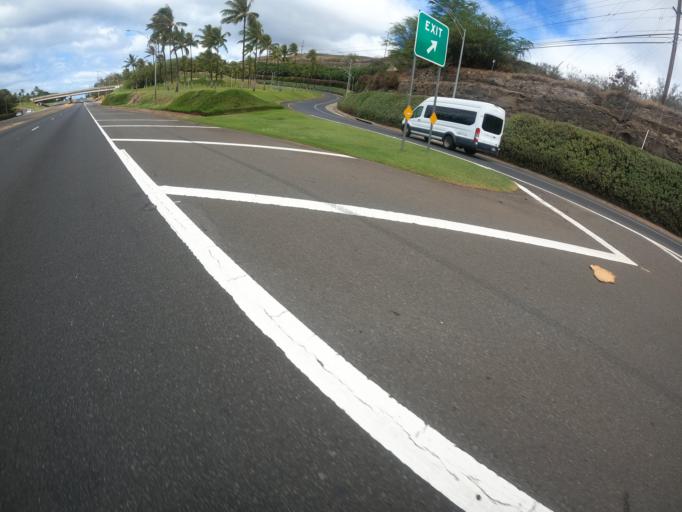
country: US
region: Hawaii
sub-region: Honolulu County
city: Makakilo
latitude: 21.3452
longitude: -158.1215
